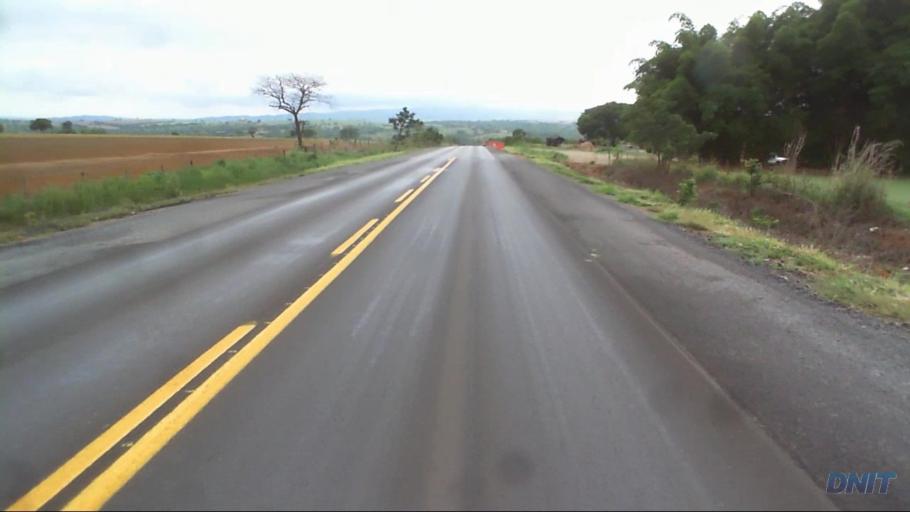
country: BR
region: Goias
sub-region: Padre Bernardo
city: Padre Bernardo
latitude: -15.2161
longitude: -48.6022
